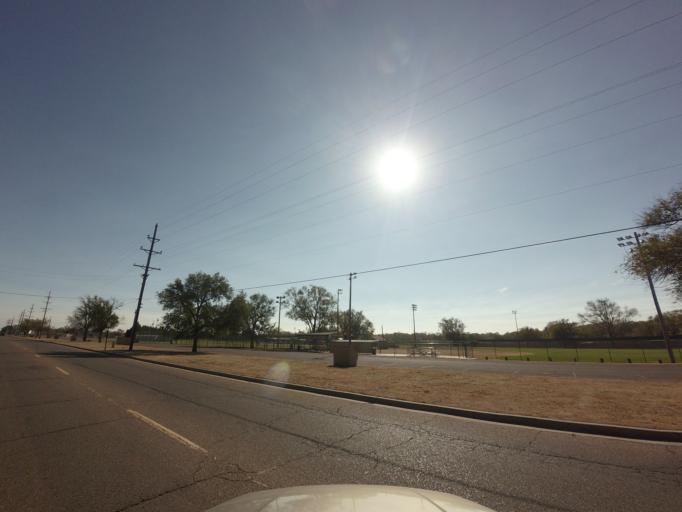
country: US
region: New Mexico
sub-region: Curry County
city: Clovis
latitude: 34.4121
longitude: -103.1842
